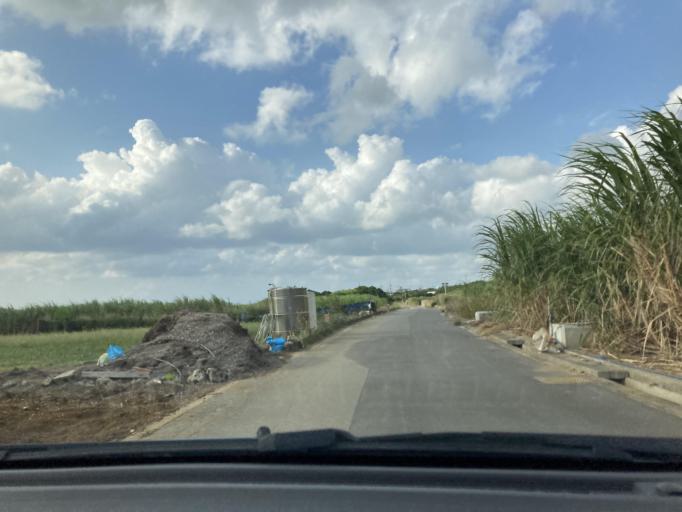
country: JP
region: Okinawa
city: Itoman
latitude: 26.0830
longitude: 127.6633
